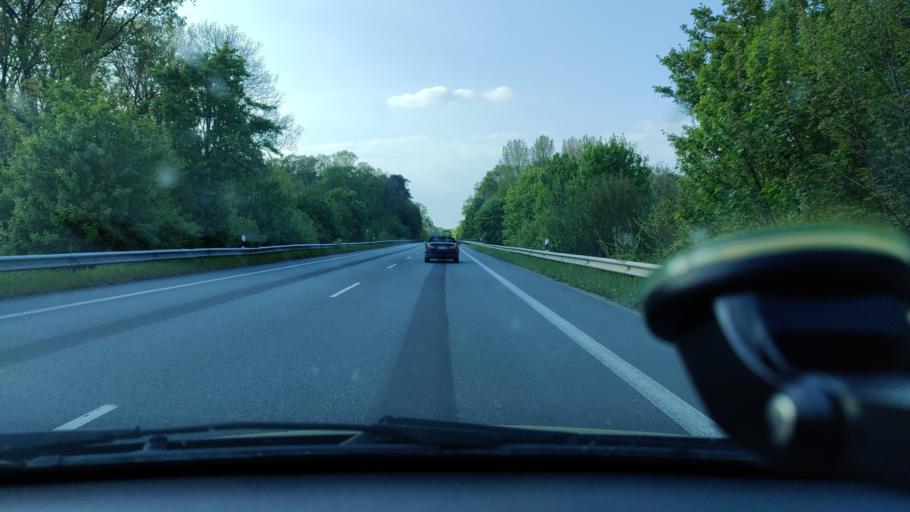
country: DE
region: North Rhine-Westphalia
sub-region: Regierungsbezirk Munster
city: Telgte
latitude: 51.9748
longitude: 7.8196
